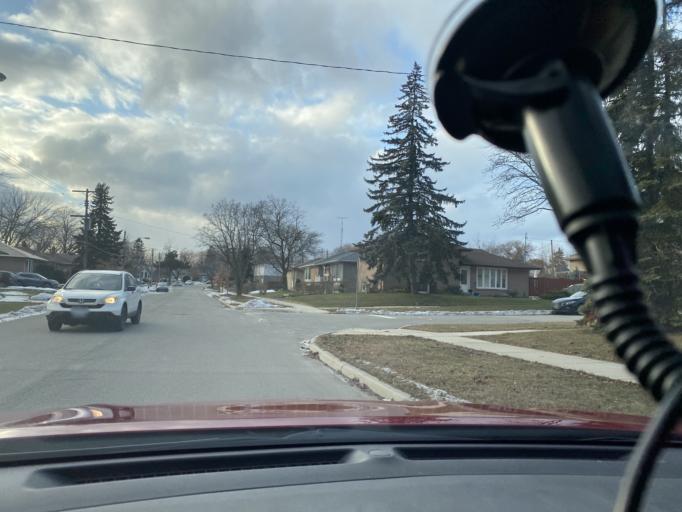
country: CA
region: Ontario
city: Scarborough
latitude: 43.7687
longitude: -79.2133
